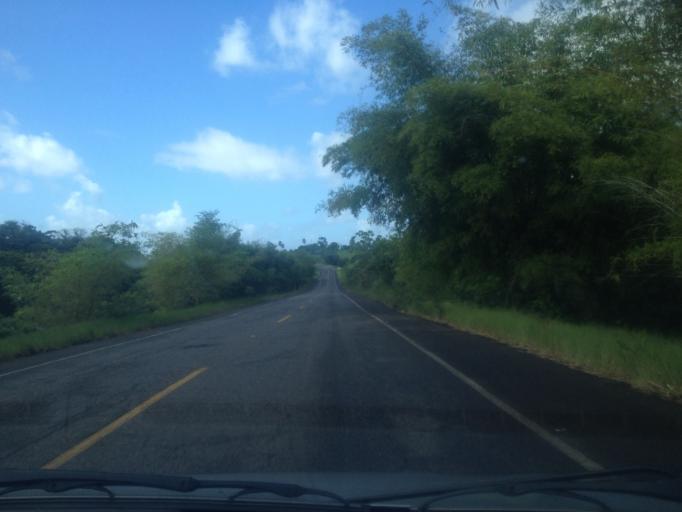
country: BR
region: Bahia
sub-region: Conde
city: Conde
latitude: -12.0559
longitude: -37.7282
